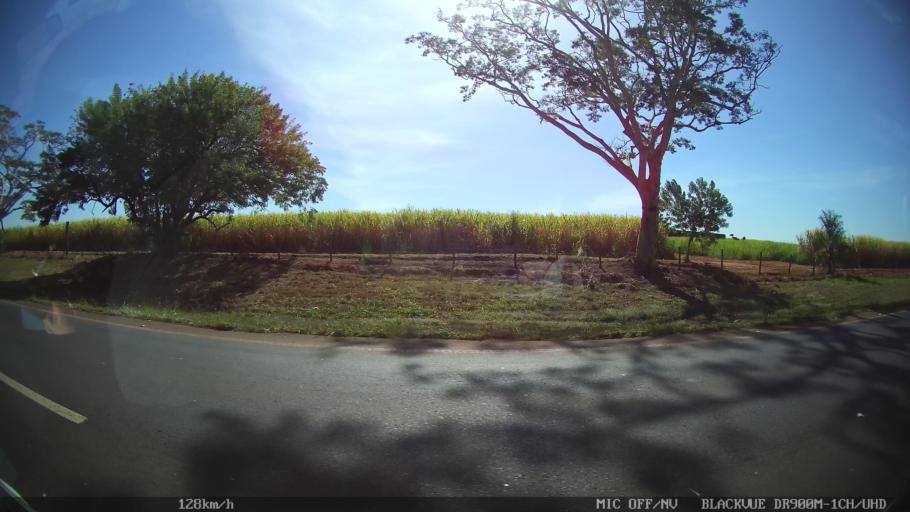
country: BR
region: Sao Paulo
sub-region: Barretos
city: Barretos
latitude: -20.5650
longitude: -48.6603
